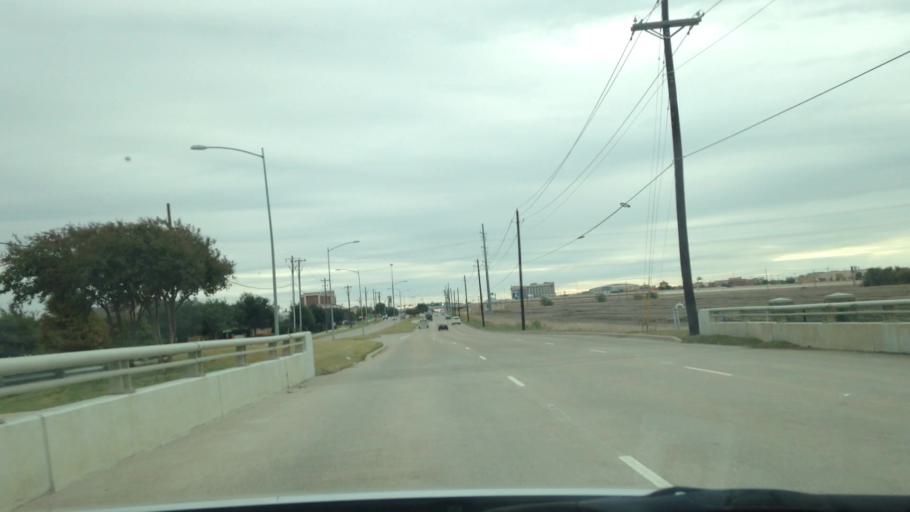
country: US
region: Texas
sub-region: Collin County
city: Allen
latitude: 33.1299
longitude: -96.6689
